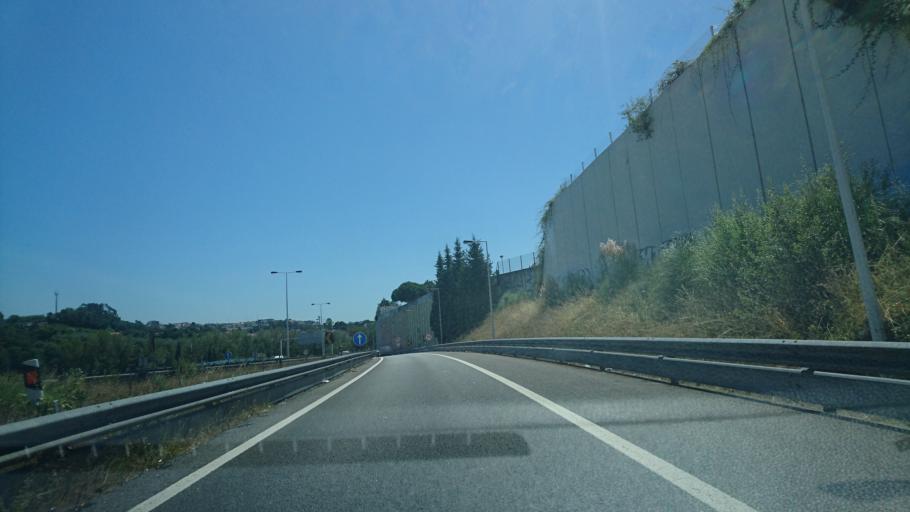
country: PT
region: Porto
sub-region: Gondomar
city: Valbom
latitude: 41.1563
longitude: -8.5725
